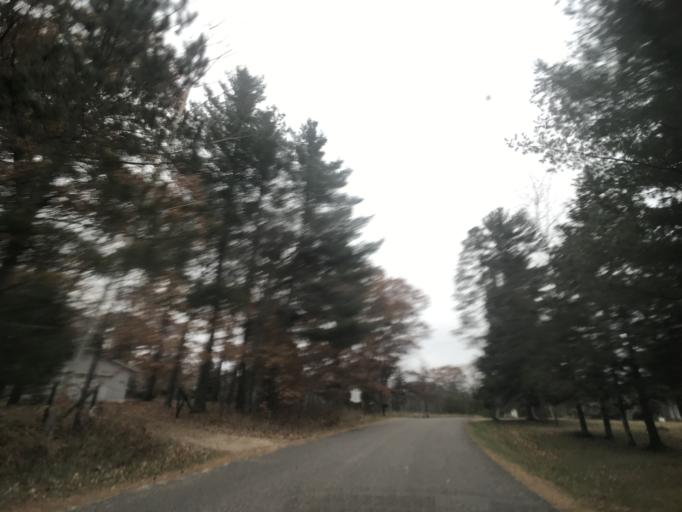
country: US
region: Michigan
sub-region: Dickinson County
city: Kingsford
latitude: 45.3850
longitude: -88.3220
